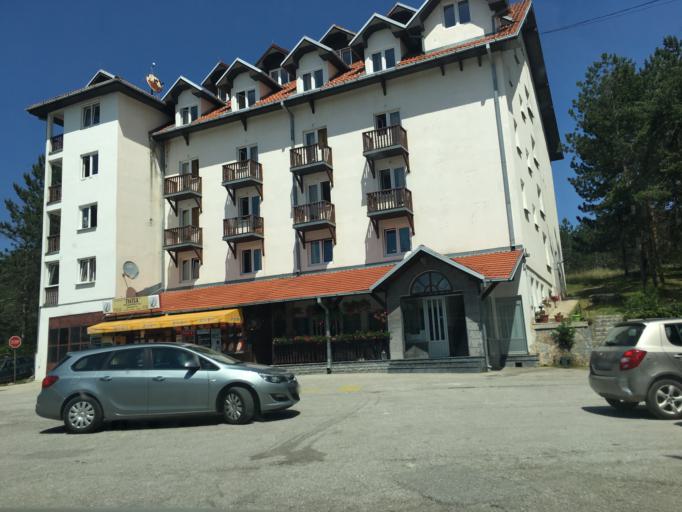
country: RS
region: Central Serbia
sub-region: Zlatiborski Okrug
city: Kosjeric
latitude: 44.1018
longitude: 19.9912
